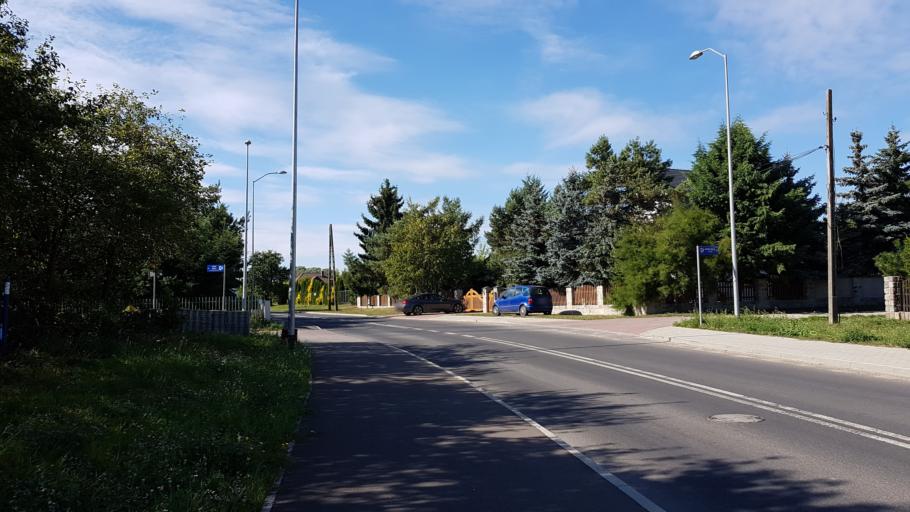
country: PL
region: West Pomeranian Voivodeship
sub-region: Powiat policki
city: Przeclaw
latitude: 53.3517
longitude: 14.4726
